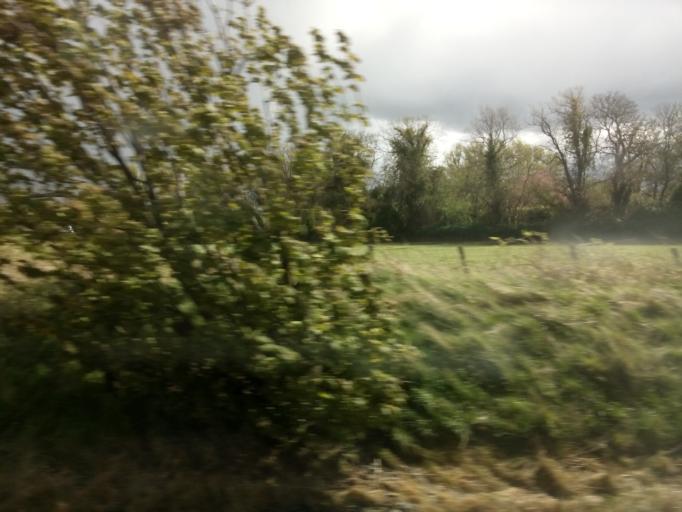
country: GB
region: Scotland
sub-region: East Lothian
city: Gullane
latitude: 56.0008
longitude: -2.8088
